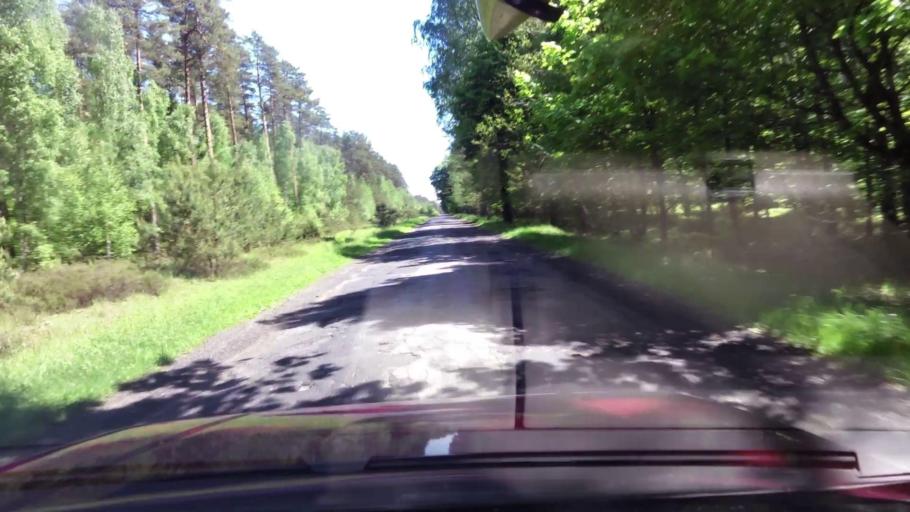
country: PL
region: West Pomeranian Voivodeship
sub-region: Powiat koszalinski
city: Sianow
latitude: 54.0772
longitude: 16.4066
